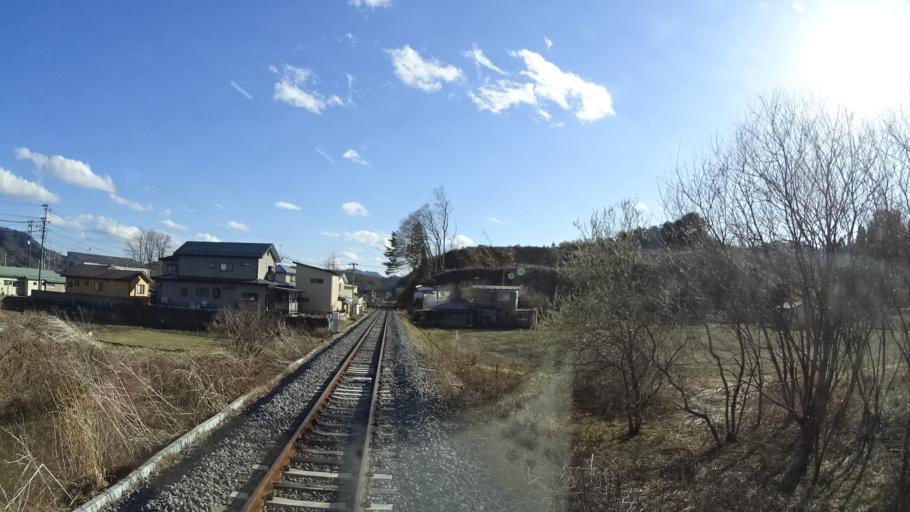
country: JP
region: Iwate
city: Miyako
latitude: 39.5752
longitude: 141.9341
